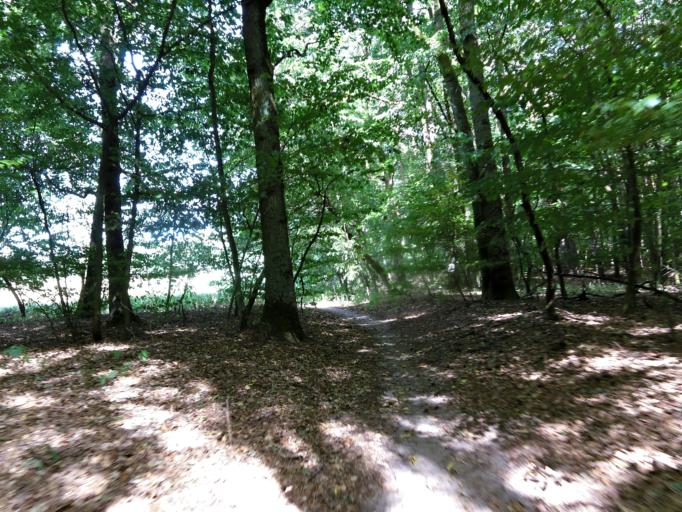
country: DE
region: Bavaria
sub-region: Regierungsbezirk Unterfranken
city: Theilheim
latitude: 49.7467
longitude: 10.0141
